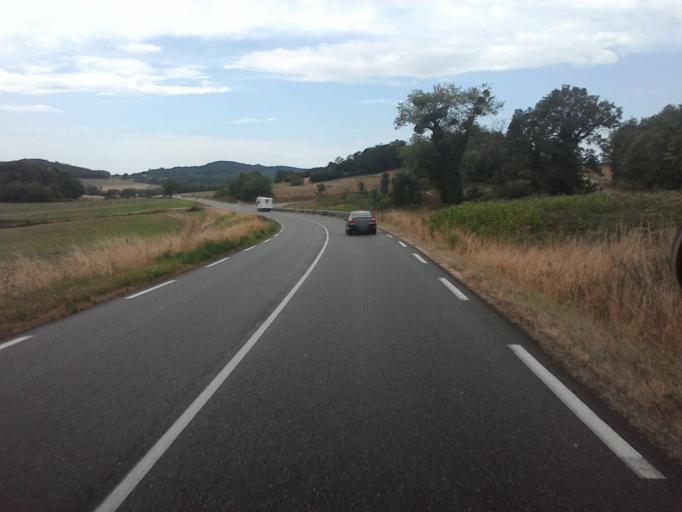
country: FR
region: Franche-Comte
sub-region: Departement du Jura
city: Poligny
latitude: 46.8252
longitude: 5.5957
